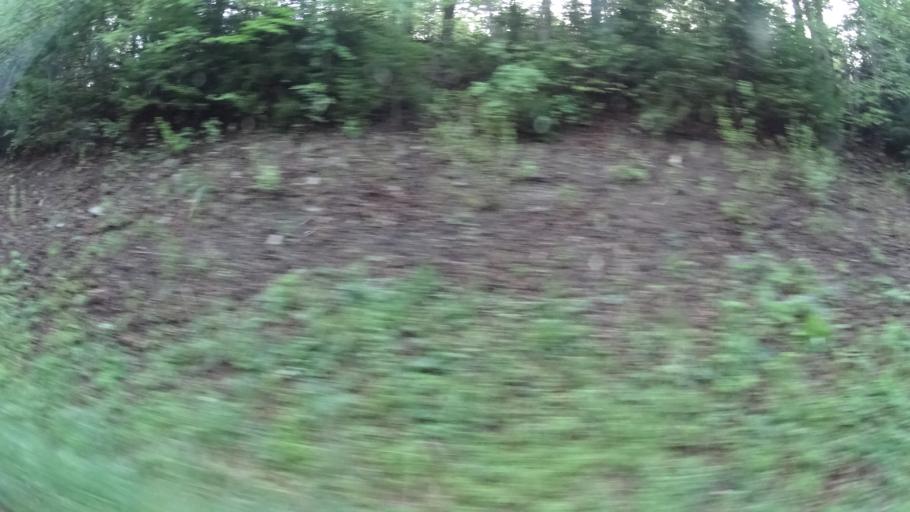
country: DE
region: Baden-Wuerttemberg
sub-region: Karlsruhe Region
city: Empfingen
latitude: 48.4356
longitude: 8.7708
